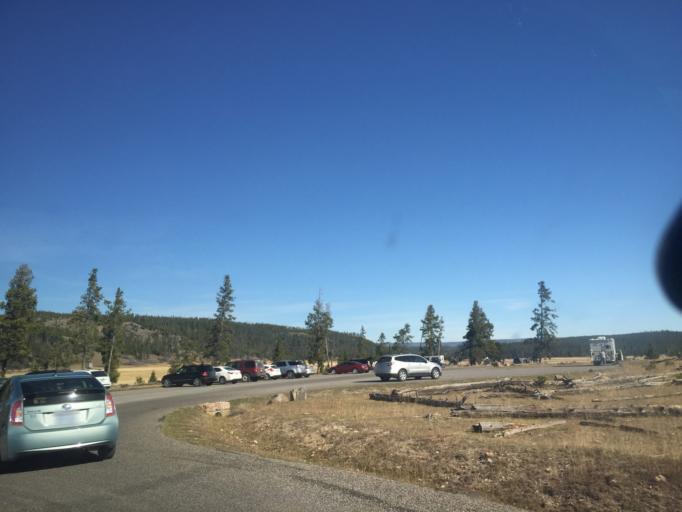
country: US
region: Montana
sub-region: Gallatin County
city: West Yellowstone
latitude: 44.5673
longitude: -110.8348
